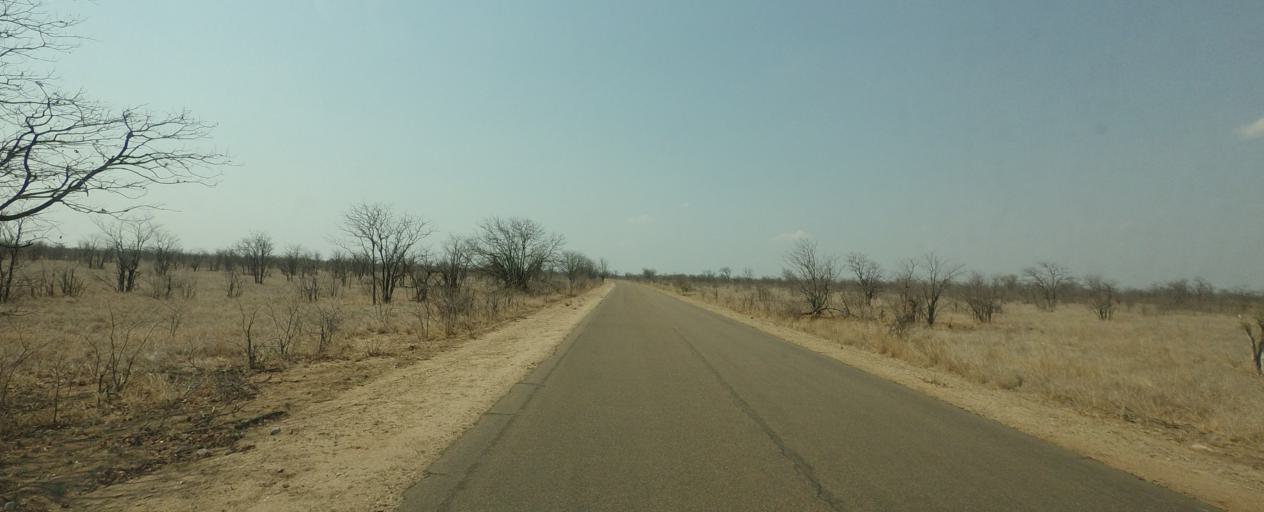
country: ZA
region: Limpopo
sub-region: Mopani District Municipality
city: Giyani
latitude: -23.3435
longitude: 31.3208
